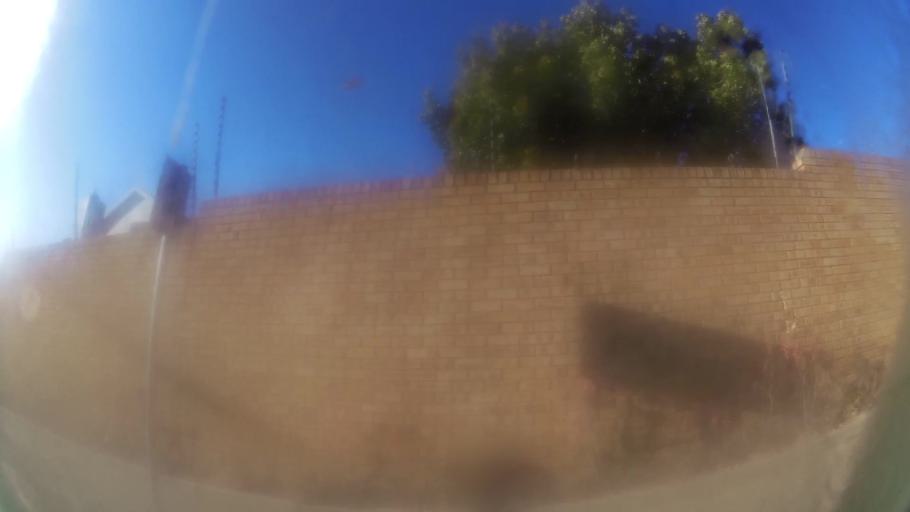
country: ZA
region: Gauteng
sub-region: City of Tshwane Metropolitan Municipality
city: Centurion
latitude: -25.8964
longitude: 28.1139
